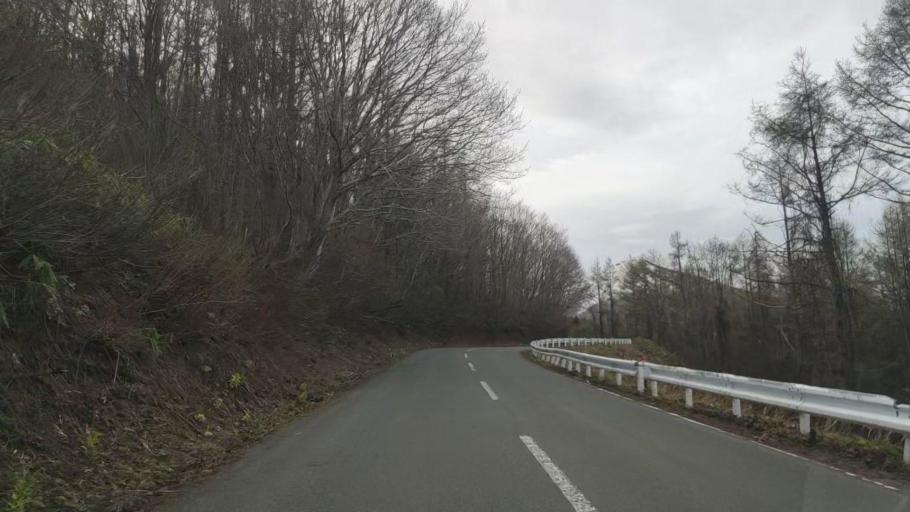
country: JP
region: Aomori
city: Aomori Shi
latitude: 40.7169
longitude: 140.8681
